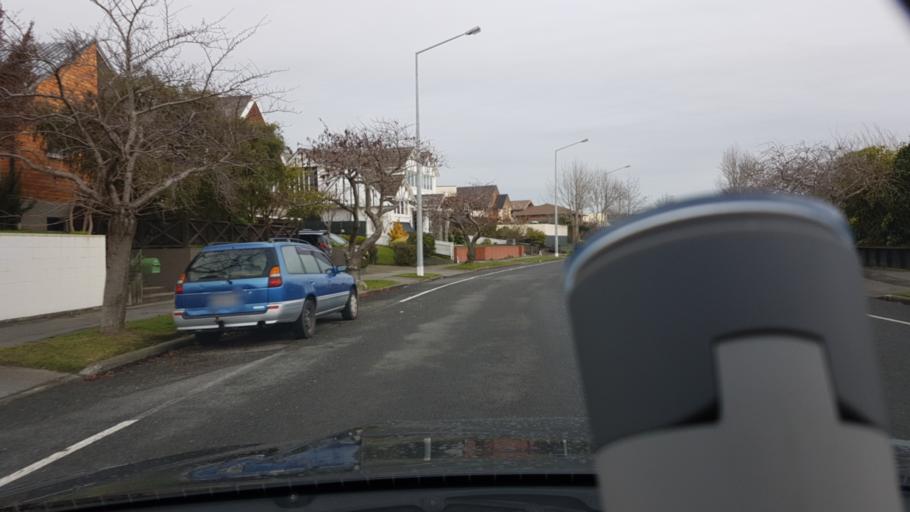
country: NZ
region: Canterbury
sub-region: Selwyn District
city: Prebbleton
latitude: -43.5168
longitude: 172.5563
